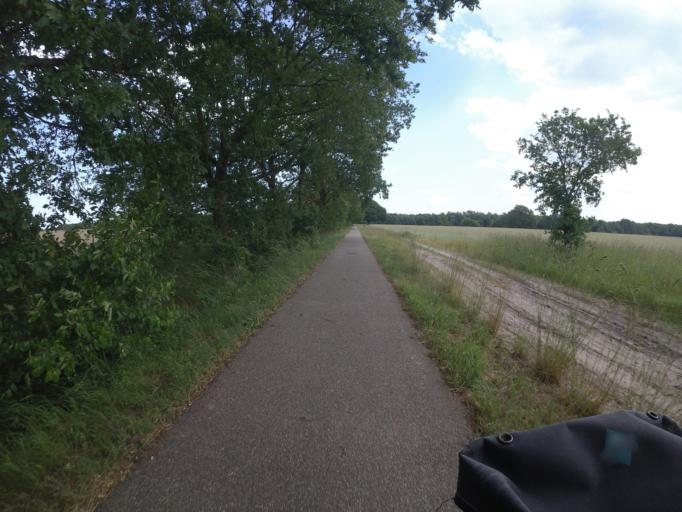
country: NL
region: Drenthe
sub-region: Gemeente Westerveld
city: Dwingeloo
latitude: 52.9090
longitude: 6.4654
